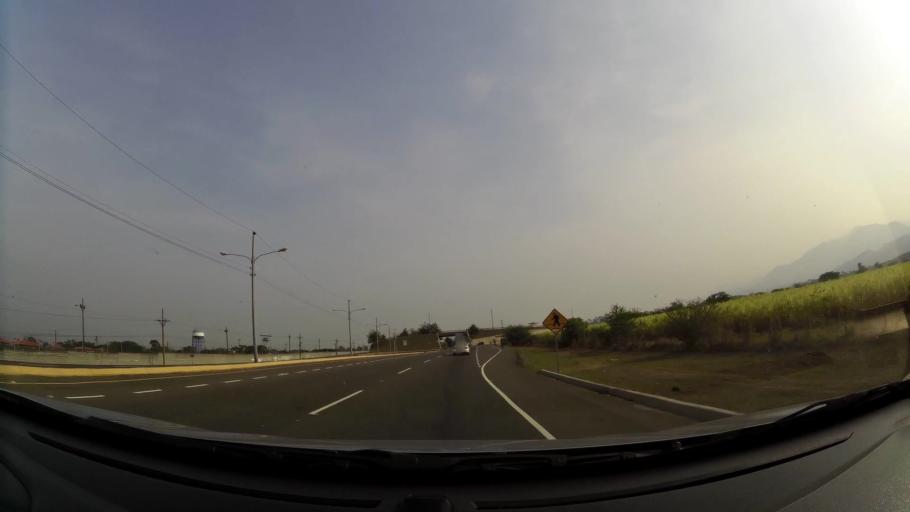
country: HN
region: La Paz
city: Yarumela
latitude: 14.3782
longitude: -87.6084
